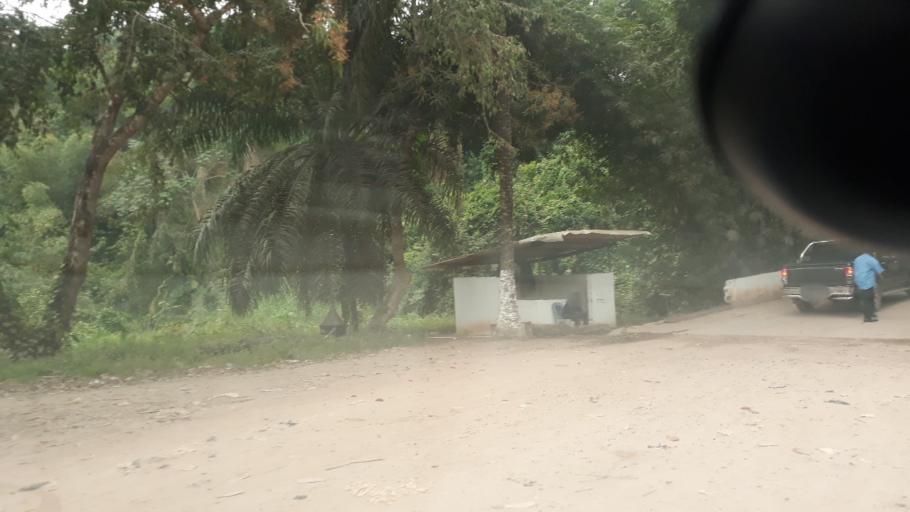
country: CD
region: Bas-Congo
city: Kasangulu
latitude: -4.4847
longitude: 15.2678
